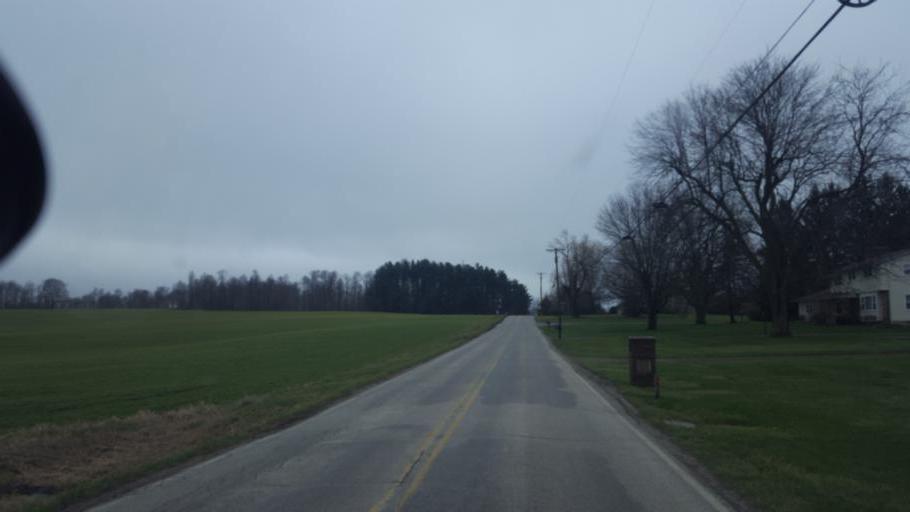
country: US
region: Ohio
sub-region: Richland County
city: Lexington
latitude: 40.6920
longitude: -82.5353
